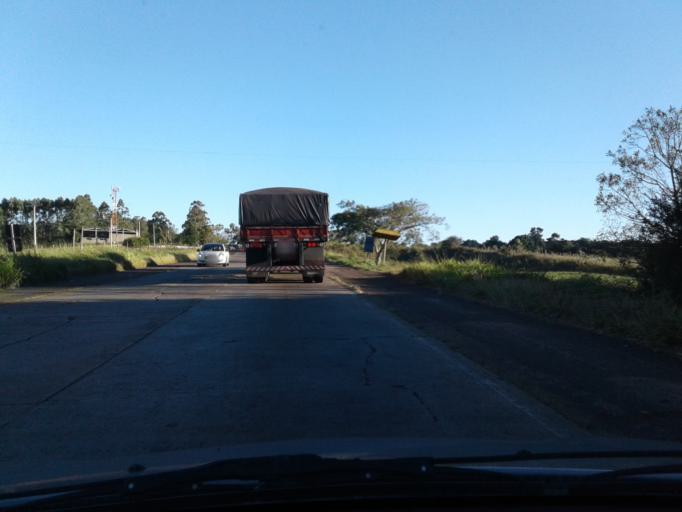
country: BR
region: Rio Grande do Sul
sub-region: Viamao
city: Viamao
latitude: -30.0318
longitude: -50.9946
